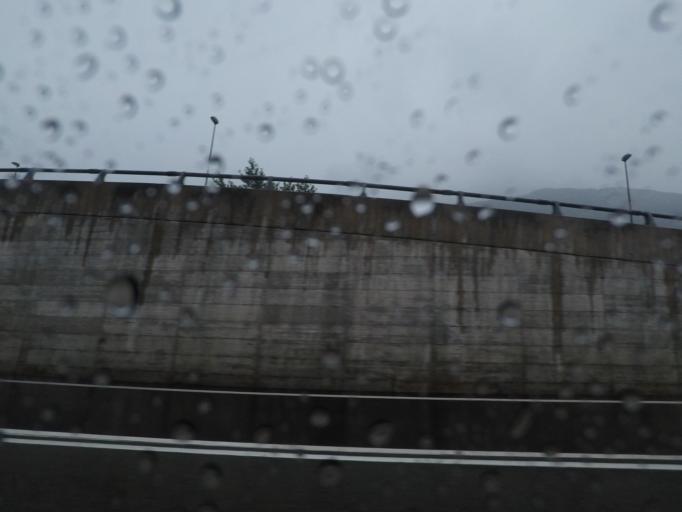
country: IT
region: Aosta Valley
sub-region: Valle d'Aosta
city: Aymavilles
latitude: 45.6985
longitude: 7.2610
